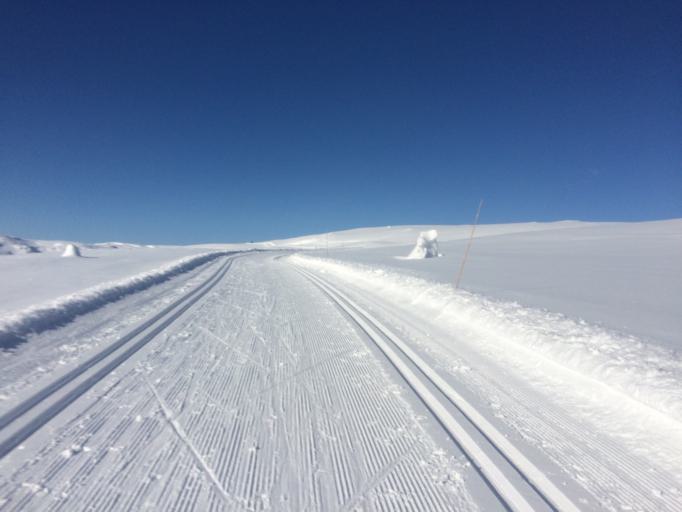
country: NO
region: Oppland
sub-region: Ringebu
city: Ringebu
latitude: 61.3679
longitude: 10.0746
